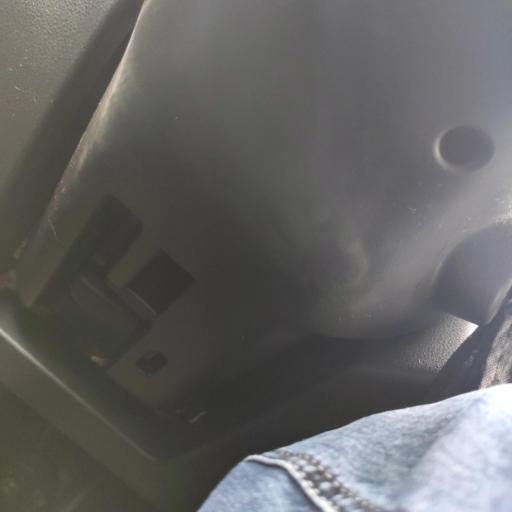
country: RU
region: Samara
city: Smyshlyayevka
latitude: 53.2119
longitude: 50.3270
